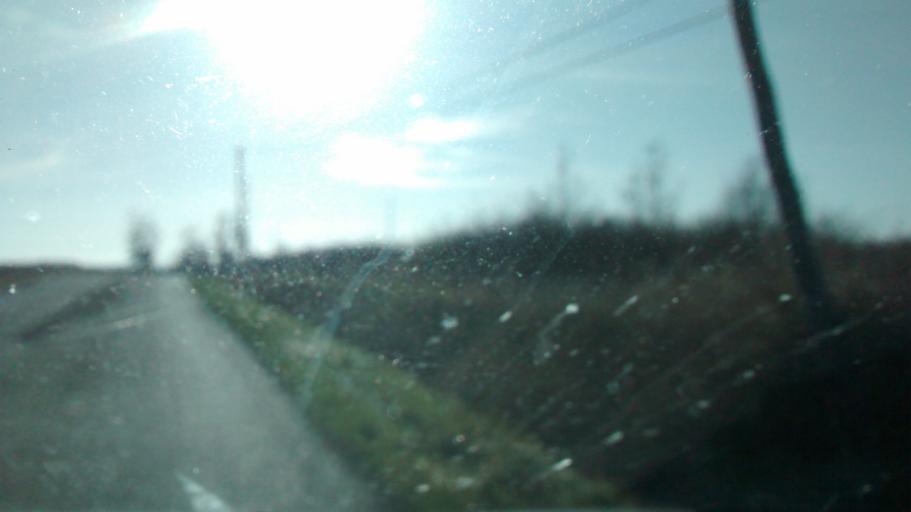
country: FR
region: Centre
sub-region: Departement d'Indre-et-Loire
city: Nazelles-Negron
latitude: 47.4472
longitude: 0.9516
